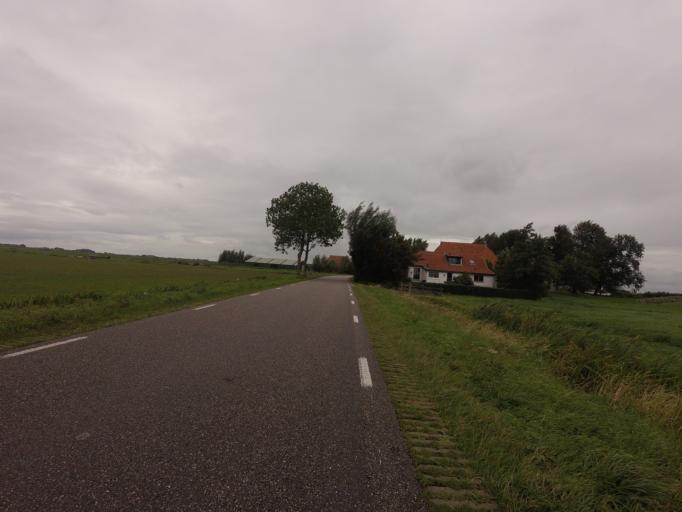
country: NL
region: Friesland
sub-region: Sudwest Fryslan
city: Heeg
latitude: 52.9673
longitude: 5.5745
